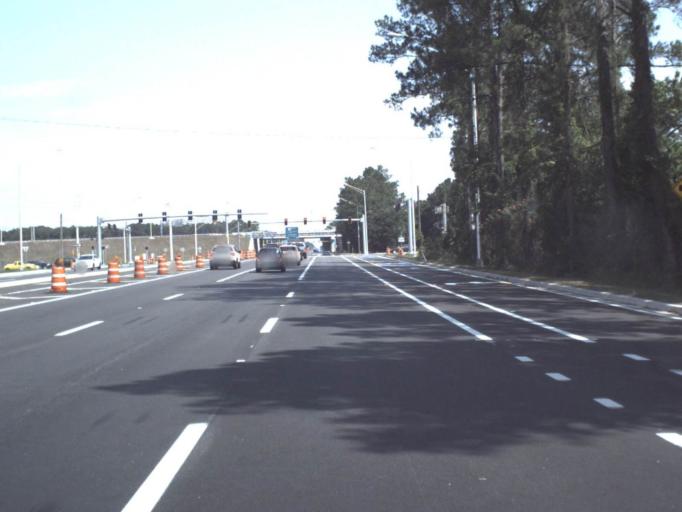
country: US
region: Florida
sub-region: Saint Johns County
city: Palm Valley
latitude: 30.1382
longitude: -81.5130
